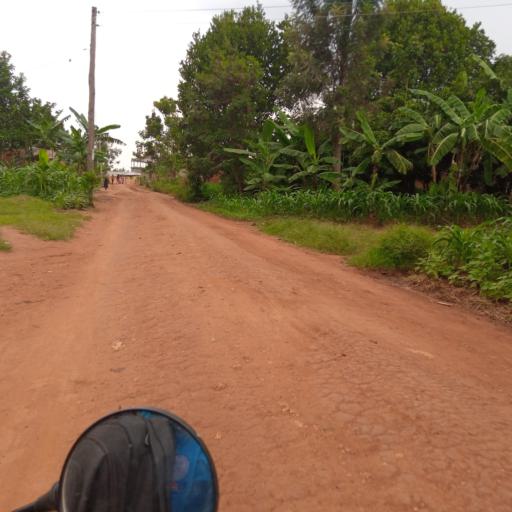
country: UG
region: Eastern Region
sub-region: Mbale District
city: Mbale
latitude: 1.1234
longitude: 34.1706
